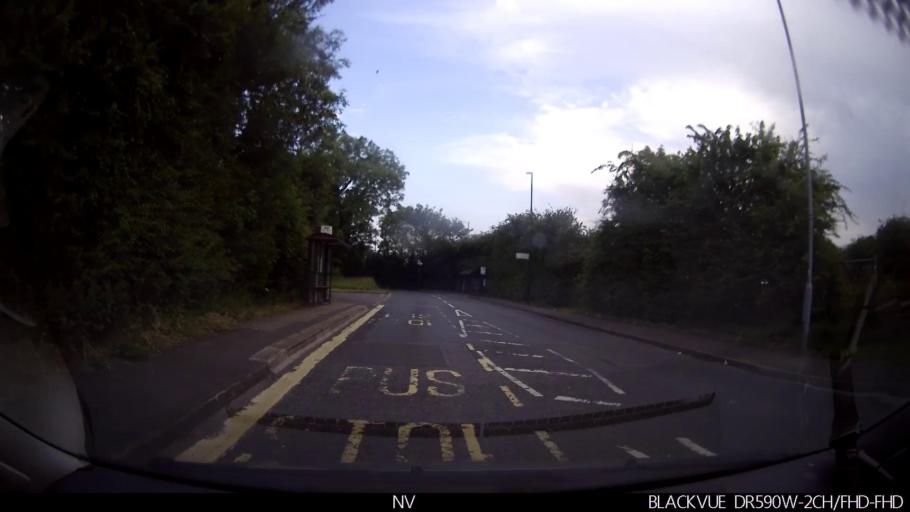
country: GB
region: England
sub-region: City of York
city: Copmanthorpe
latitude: 53.9442
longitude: -1.1408
